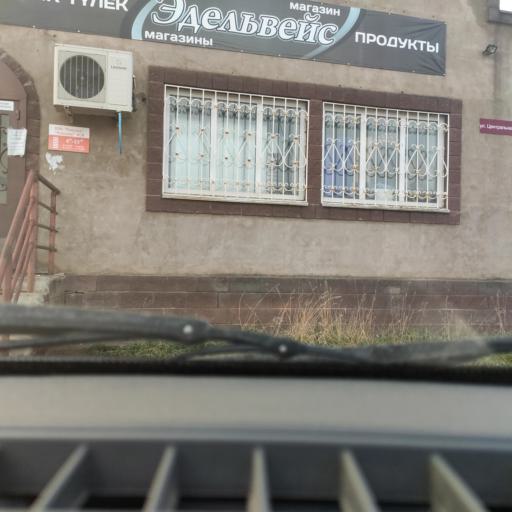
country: RU
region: Bashkortostan
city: Avdon
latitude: 54.6543
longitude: 55.7734
